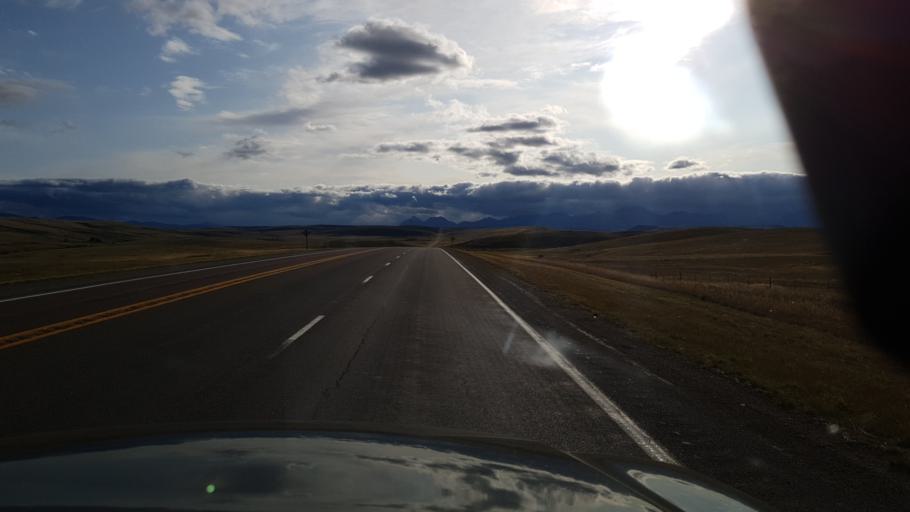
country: US
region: Montana
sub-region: Glacier County
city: South Browning
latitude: 48.5408
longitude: -113.0355
